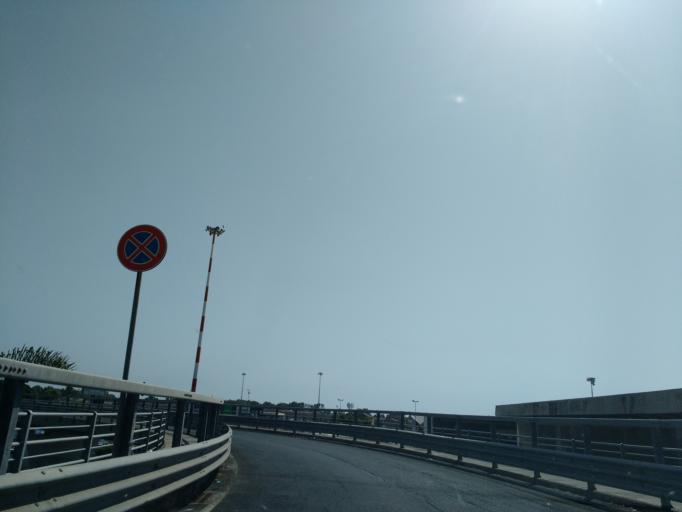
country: IT
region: Sicily
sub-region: Catania
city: Catania
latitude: 37.4704
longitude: 15.0669
